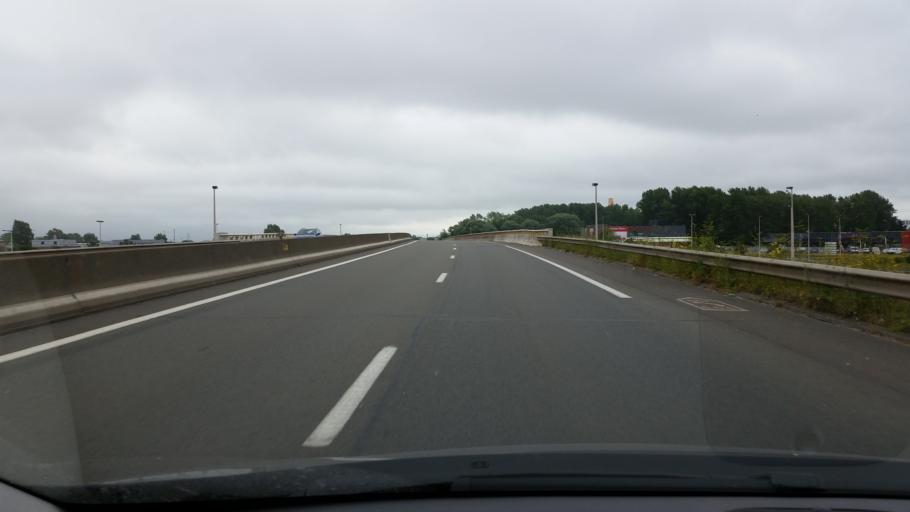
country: FR
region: Nord-Pas-de-Calais
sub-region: Departement du Pas-de-Calais
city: Marck
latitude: 50.9575
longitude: 1.9053
